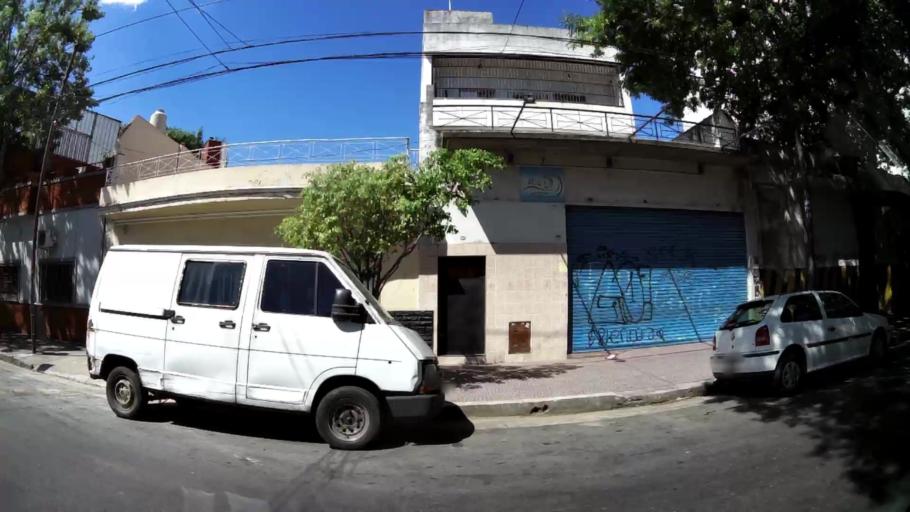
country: AR
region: Buenos Aires F.D.
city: Villa Santa Rita
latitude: -34.6315
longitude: -58.4377
